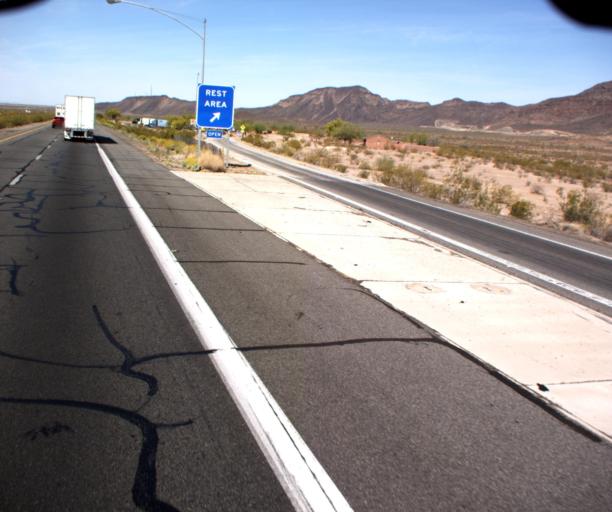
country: US
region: Arizona
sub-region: Maricopa County
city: Buckeye
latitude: 33.5199
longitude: -113.0638
